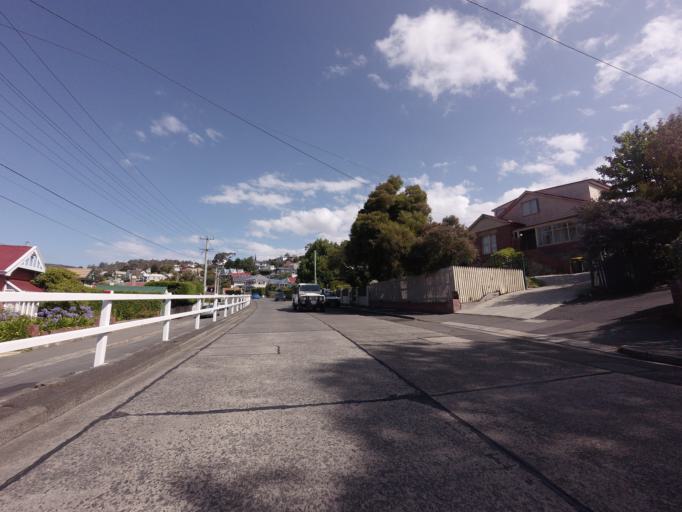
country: AU
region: Tasmania
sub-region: Hobart
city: Dynnyrne
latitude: -42.8998
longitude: 147.3169
